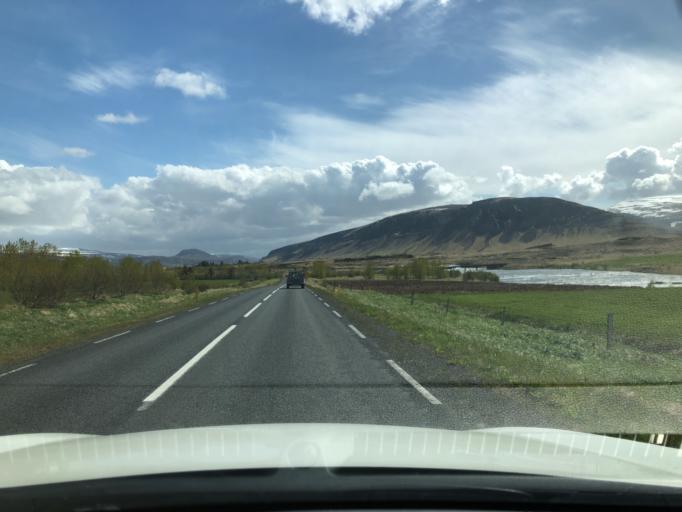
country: IS
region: Capital Region
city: Mosfellsbaer
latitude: 64.3453
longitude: -21.6163
